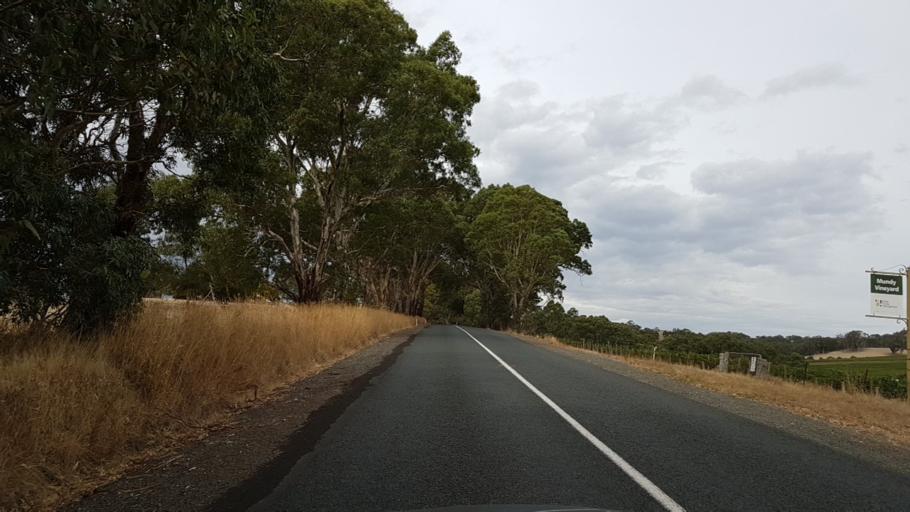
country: AU
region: South Australia
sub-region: Adelaide Hills
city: Gumeracha
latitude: -34.7823
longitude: 138.9167
